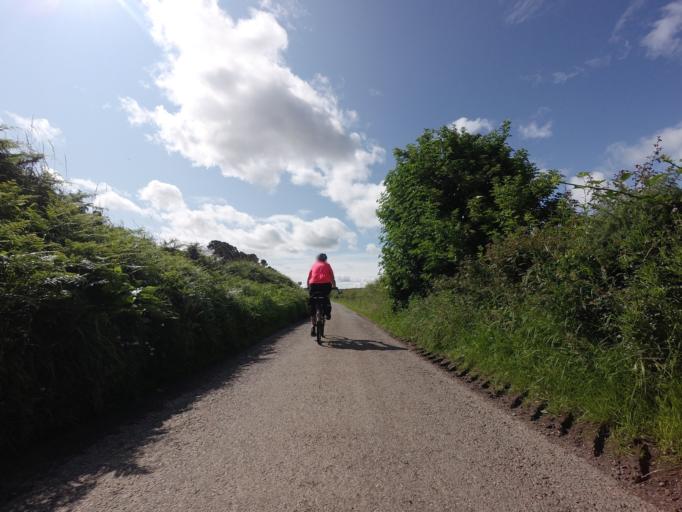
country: GB
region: Scotland
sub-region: Moray
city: Kinloss
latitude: 57.6411
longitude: -3.5215
